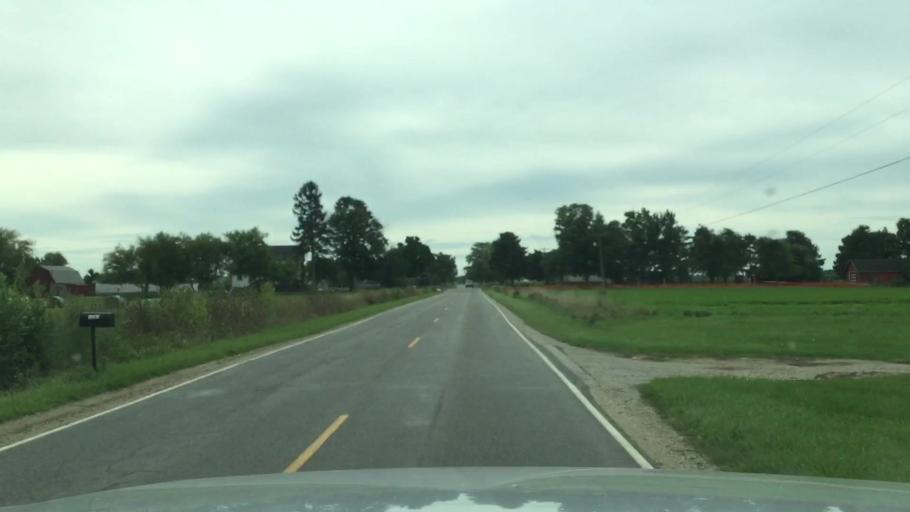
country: US
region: Michigan
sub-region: Shiawassee County
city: Durand
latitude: 43.0172
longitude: -83.9871
